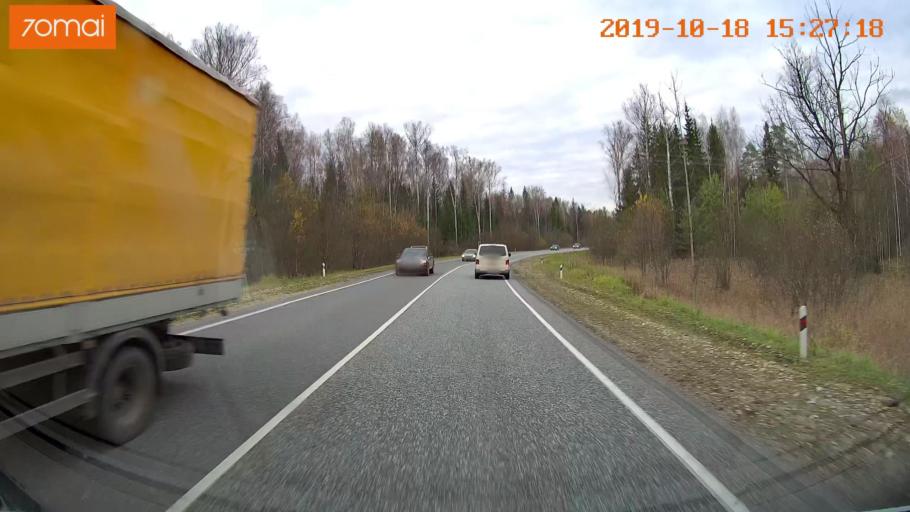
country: RU
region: Vladimir
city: Anopino
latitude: 55.7515
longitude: 40.6712
